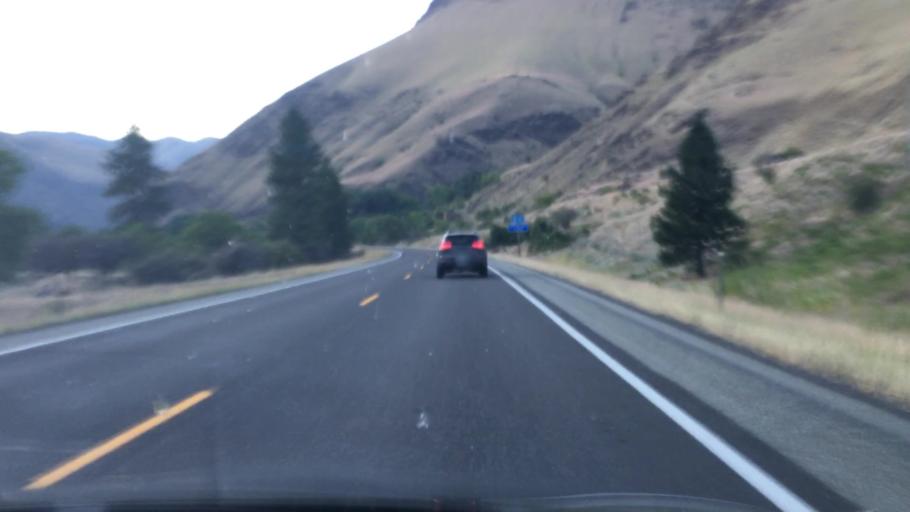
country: US
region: Idaho
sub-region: Valley County
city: McCall
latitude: 45.3371
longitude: -116.3476
